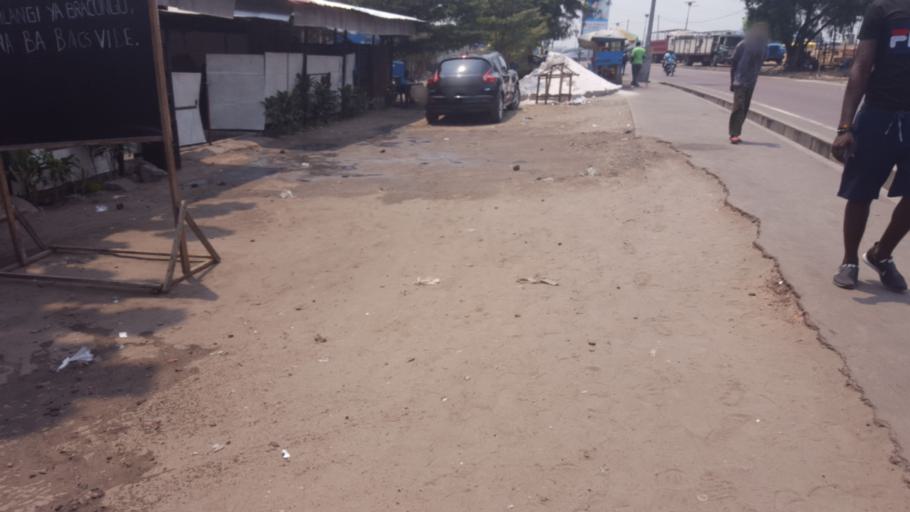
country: CD
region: Kinshasa
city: Masina
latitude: -4.3819
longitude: 15.3536
